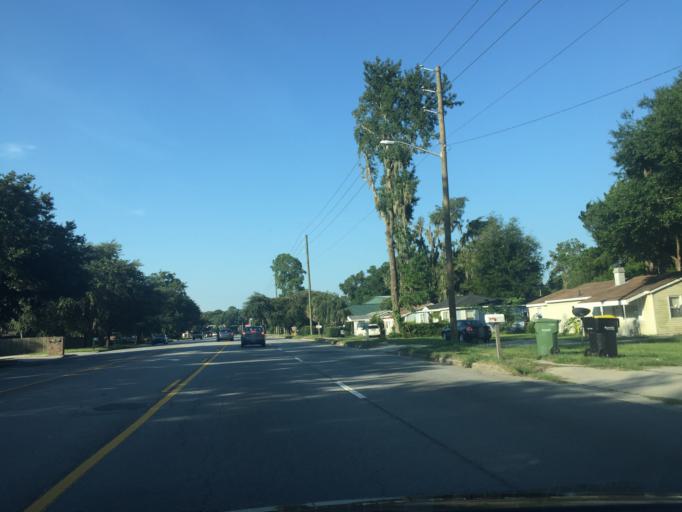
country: US
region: Georgia
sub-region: Chatham County
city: Isle of Hope
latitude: 31.9971
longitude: -81.1045
